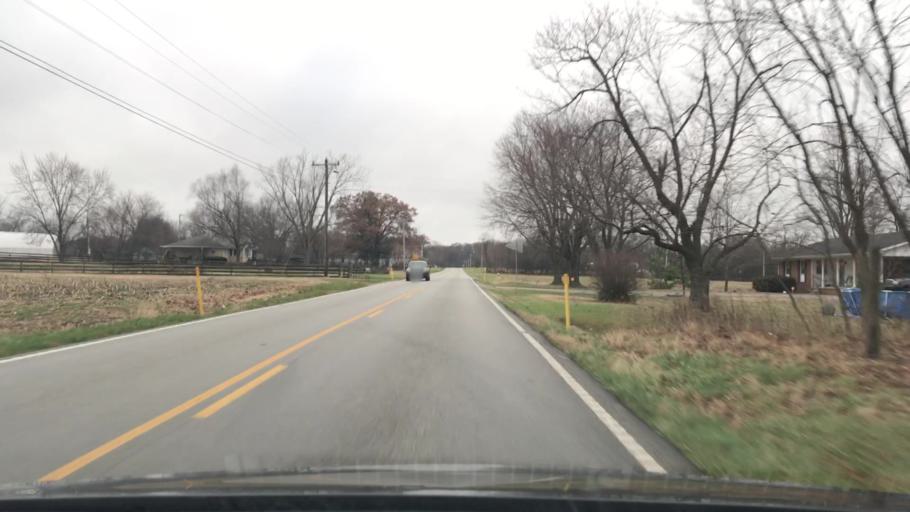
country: US
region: Kentucky
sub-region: Todd County
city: Guthrie
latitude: 36.7185
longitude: -87.1913
